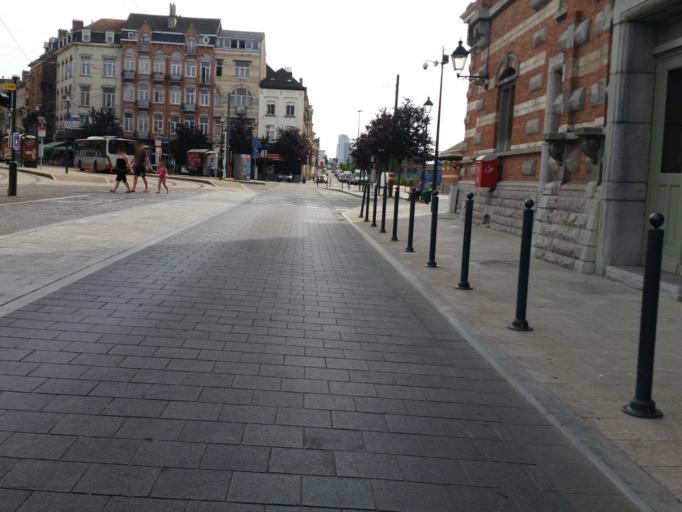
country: BE
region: Brussels Capital
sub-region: Bruxelles-Capitale
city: Brussels
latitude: 50.8780
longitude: 4.3799
